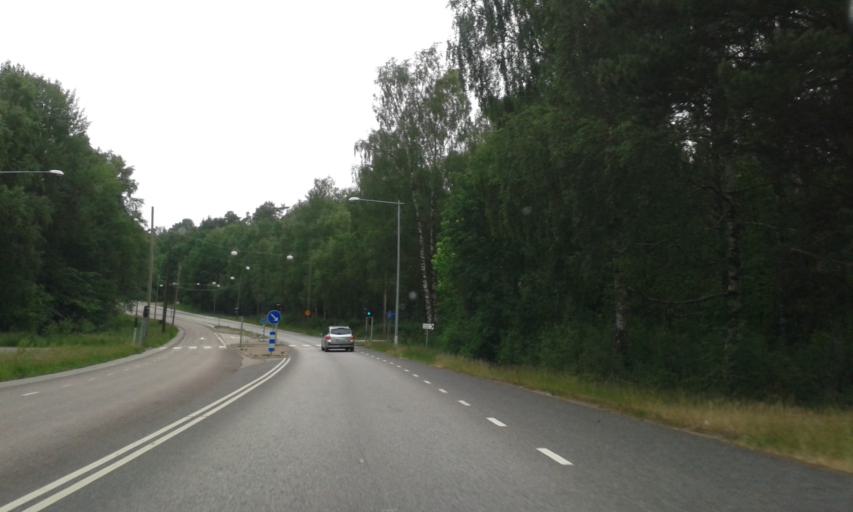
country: SE
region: Vaestra Goetaland
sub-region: Goteborg
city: Eriksbo
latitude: 57.7640
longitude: 12.0528
